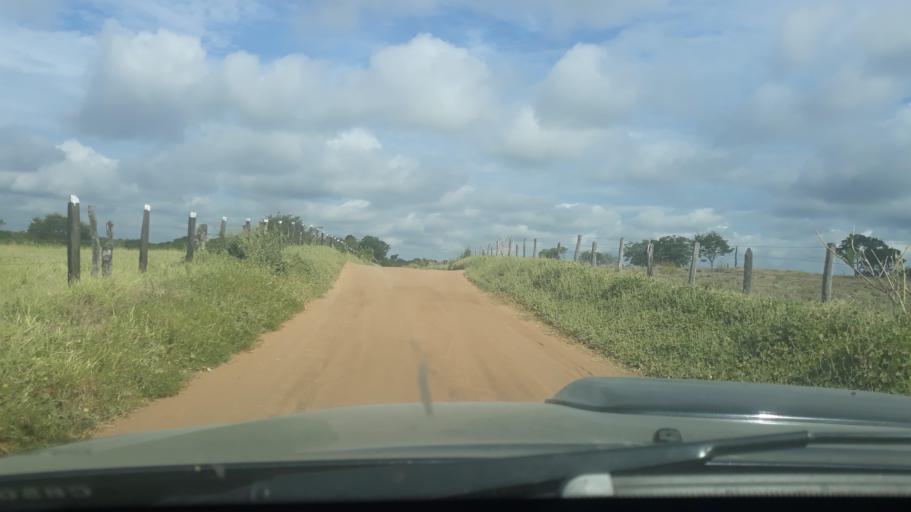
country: BR
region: Bahia
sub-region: Riacho De Santana
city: Riacho de Santana
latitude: -13.9005
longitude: -42.8680
